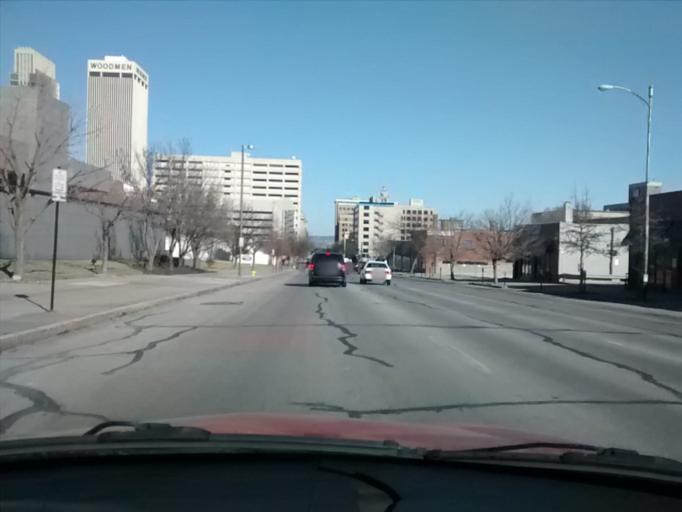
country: US
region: Nebraska
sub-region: Douglas County
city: Omaha
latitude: 41.2566
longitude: -95.9454
